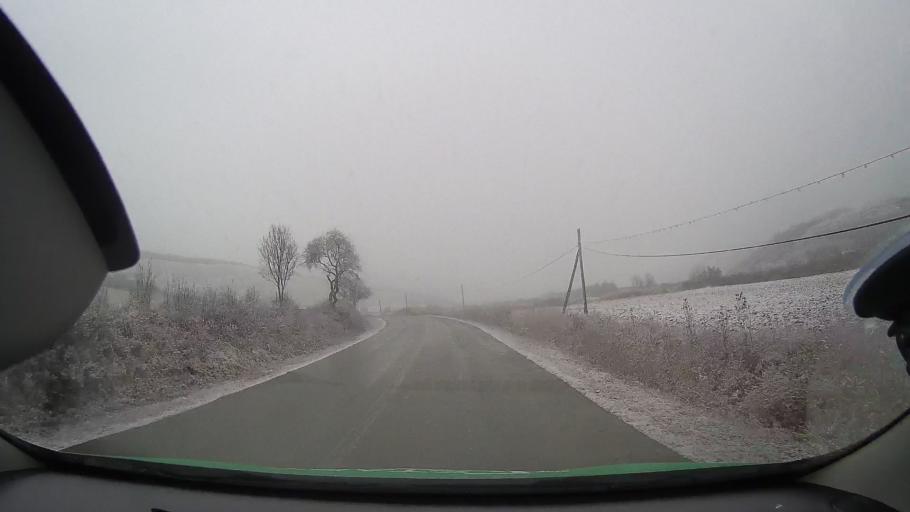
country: RO
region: Alba
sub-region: Comuna Lopadea Noua
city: Lopadea Noua
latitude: 46.2947
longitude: 23.8421
